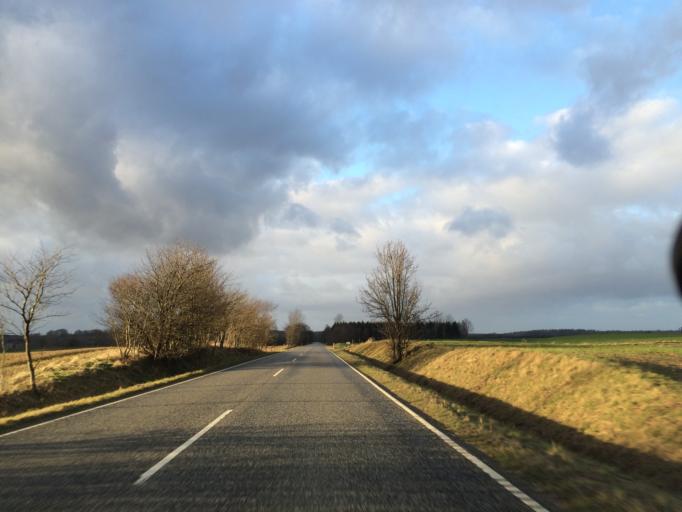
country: DK
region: Central Jutland
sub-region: Silkeborg Kommune
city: Svejbaek
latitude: 56.1012
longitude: 9.6013
